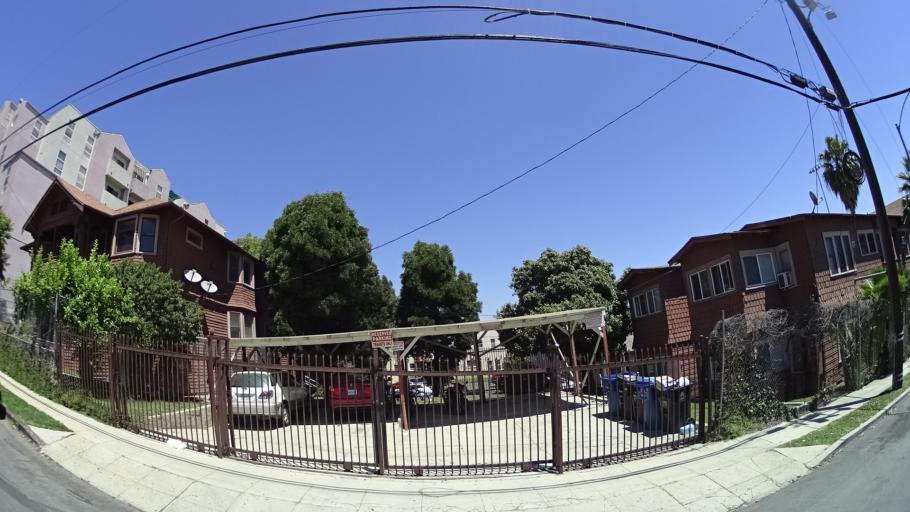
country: US
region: California
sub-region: Los Angeles County
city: Los Angeles
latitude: 34.0622
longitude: -118.2549
